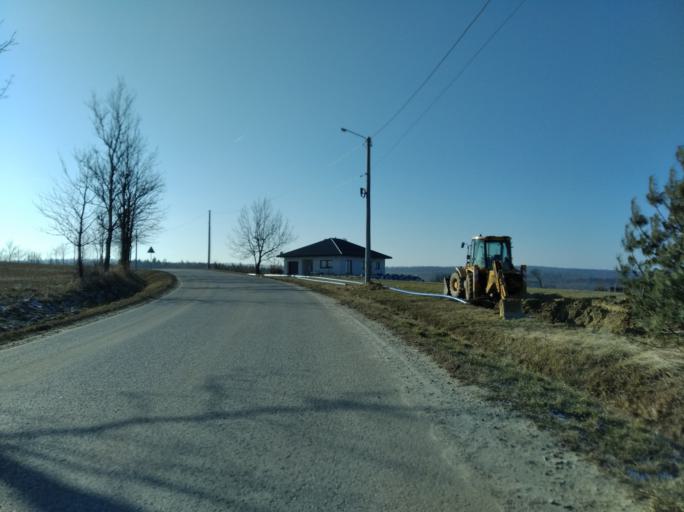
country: PL
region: Subcarpathian Voivodeship
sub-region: Powiat rzeszowski
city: Straszydle
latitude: 49.8816
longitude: 21.9871
